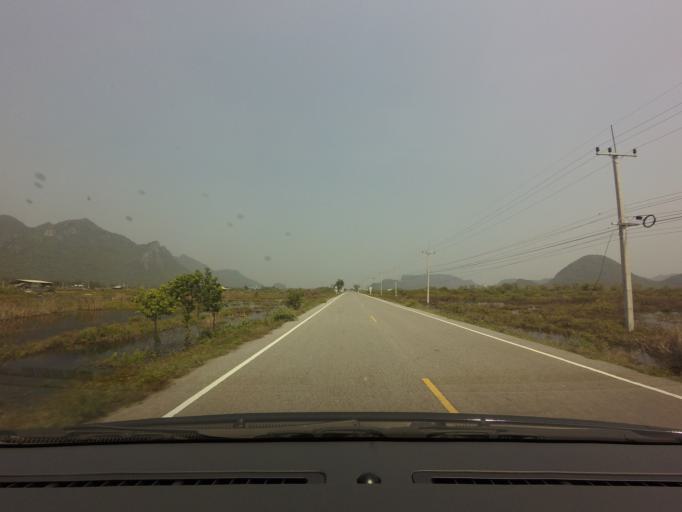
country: TH
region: Prachuap Khiri Khan
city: Sam Roi Yot
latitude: 12.1793
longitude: 99.9747
